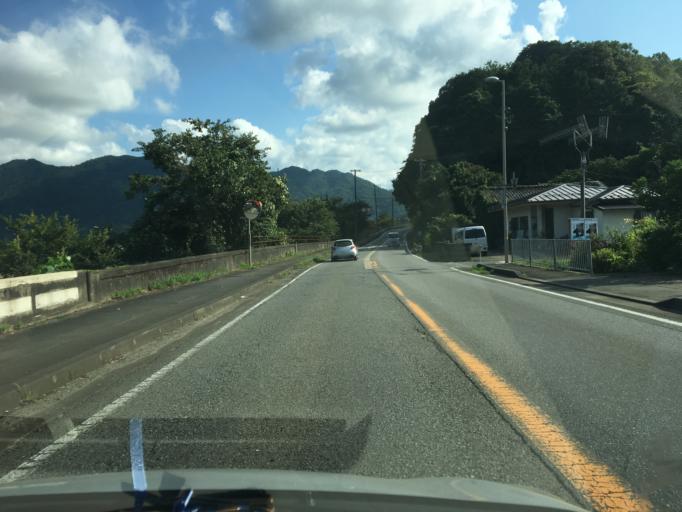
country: JP
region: Hyogo
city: Toyooka
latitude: 35.4338
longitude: 134.7889
